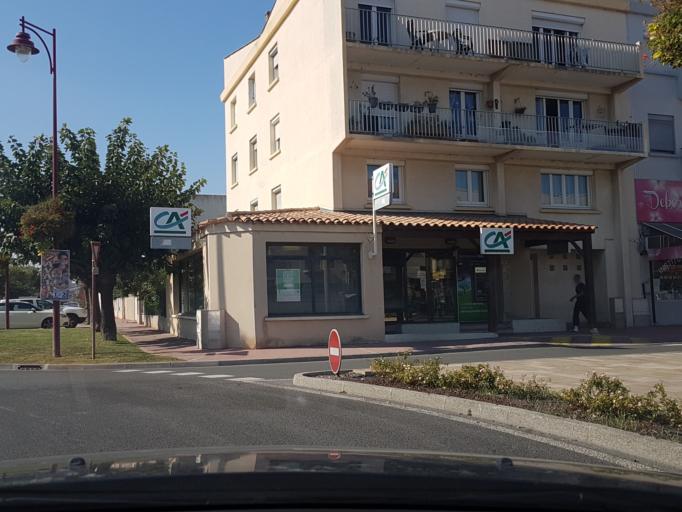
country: FR
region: Languedoc-Roussillon
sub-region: Departement de l'Aude
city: Port-la-Nouvelle
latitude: 43.0193
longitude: 3.0460
